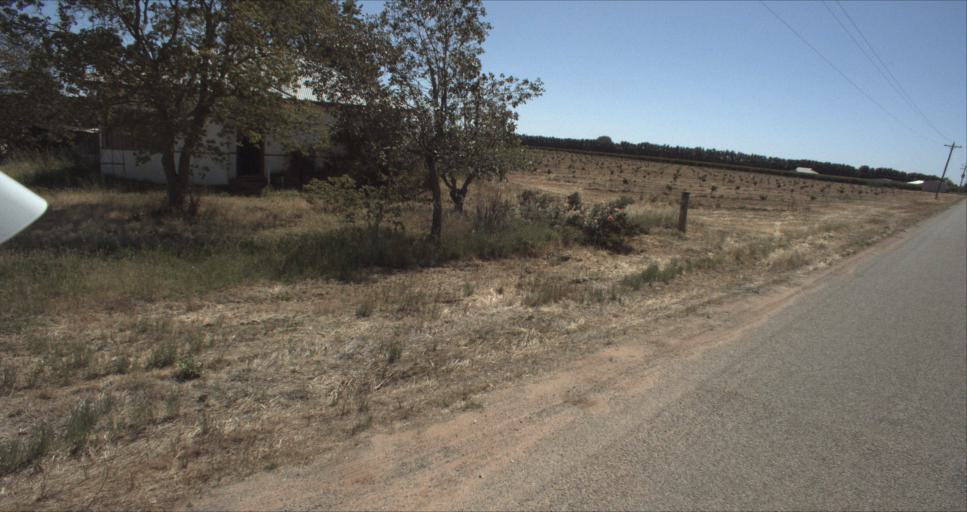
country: AU
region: New South Wales
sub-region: Leeton
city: Leeton
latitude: -34.5424
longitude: 146.3530
